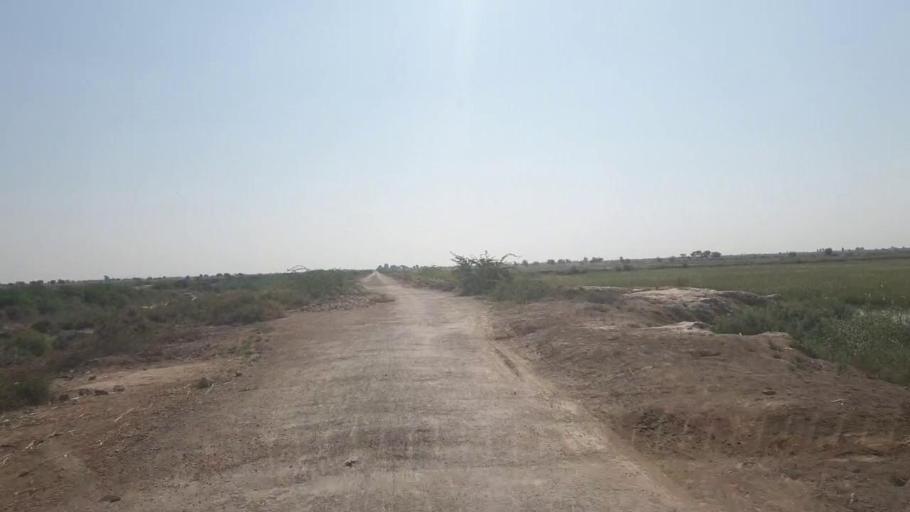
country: PK
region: Sindh
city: Tando Bago
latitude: 24.8617
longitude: 69.1643
